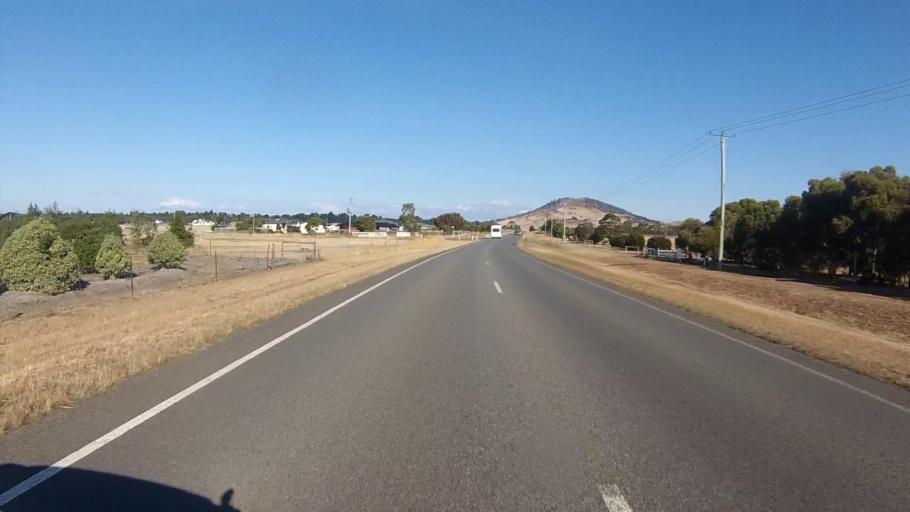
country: AU
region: Tasmania
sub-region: Clarence
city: Seven Mile Beach
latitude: -42.8480
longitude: 147.4820
